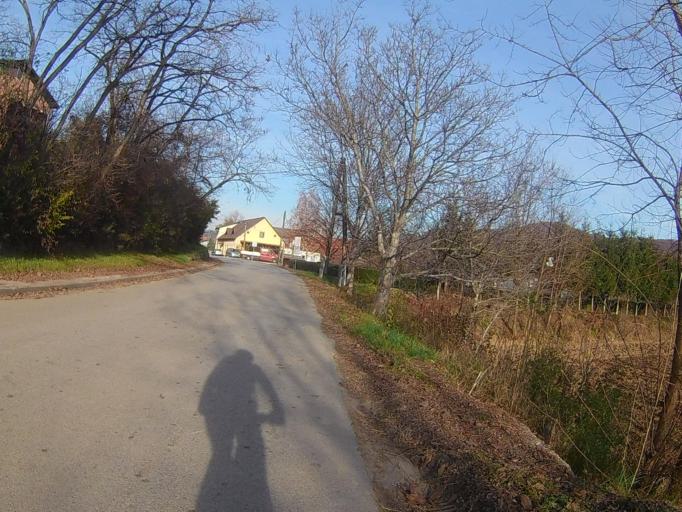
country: SI
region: Miklavz na Dravskem Polju
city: Miklavz na Dravskem Polju
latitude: 46.5209
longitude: 15.7050
